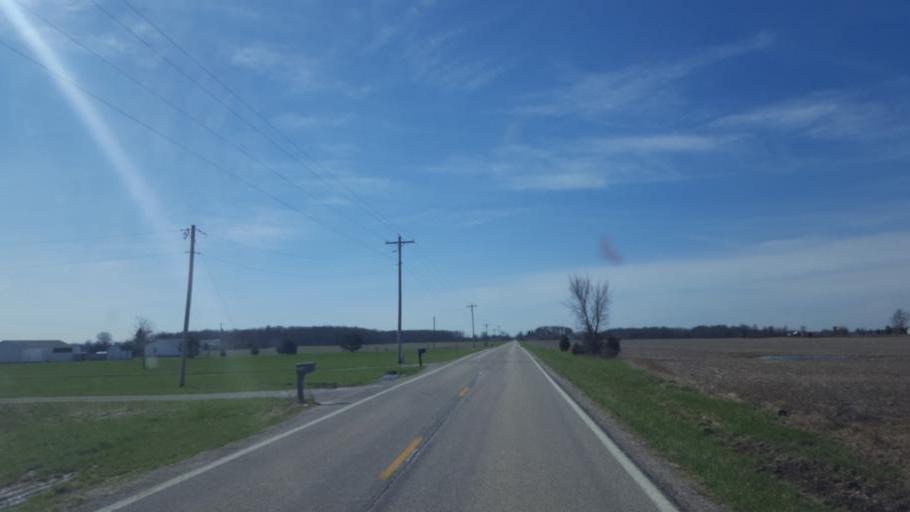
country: US
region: Ohio
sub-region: Morrow County
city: Cardington
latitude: 40.5199
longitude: -82.9627
